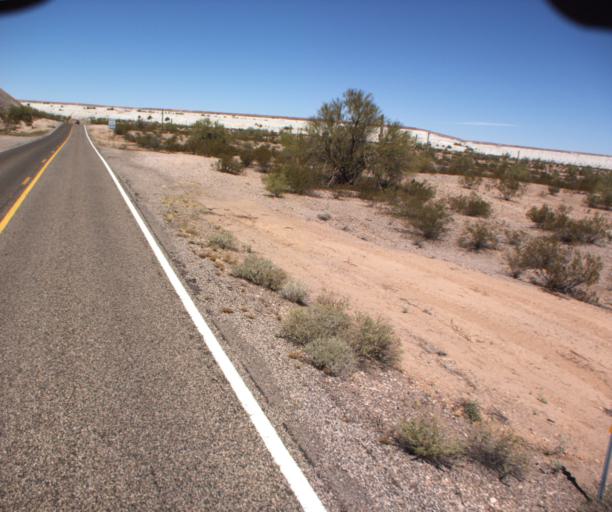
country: US
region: Arizona
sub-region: Pima County
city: Ajo
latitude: 32.3604
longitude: -112.8329
